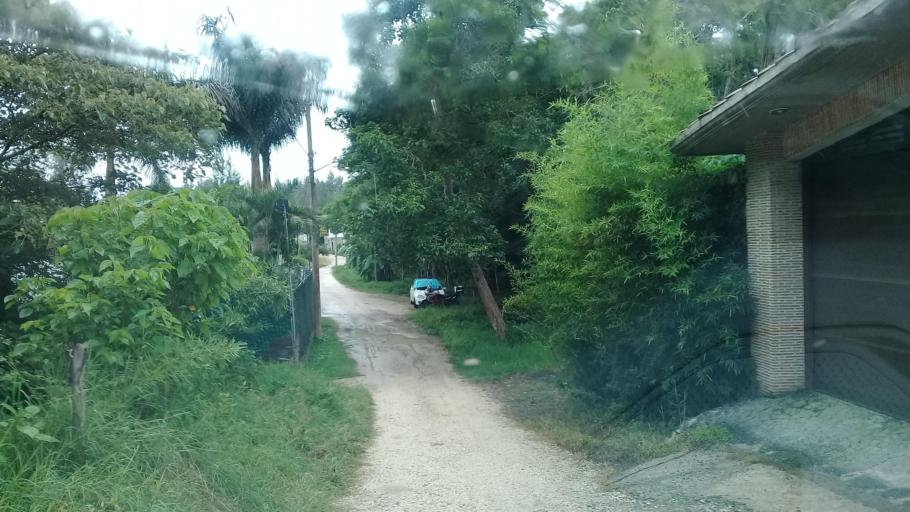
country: MX
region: Veracruz
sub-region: Emiliano Zapata
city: Jacarandas
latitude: 19.5027
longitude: -96.8419
